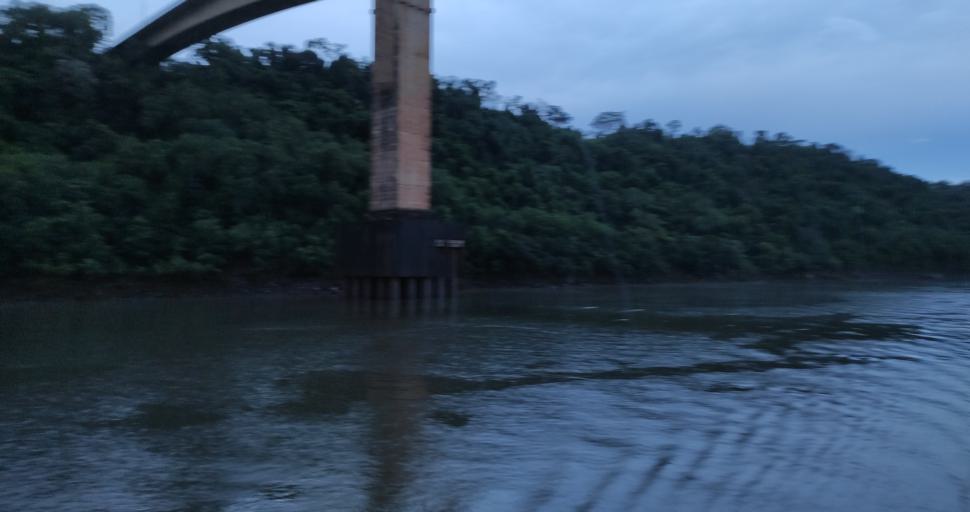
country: AR
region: Misiones
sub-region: Departamento de Iguazu
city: Puerto Iguazu
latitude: -25.5891
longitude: -54.5623
